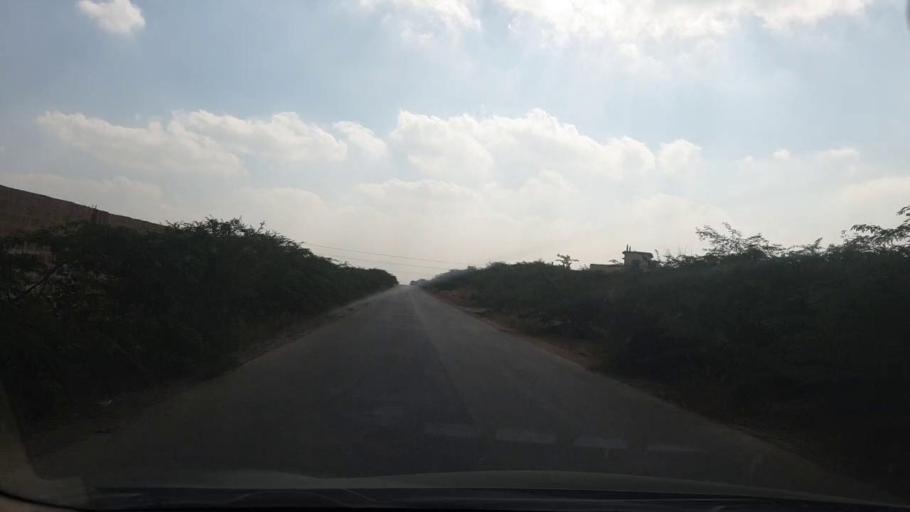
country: PK
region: Sindh
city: Malir Cantonment
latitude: 25.0138
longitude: 67.3526
